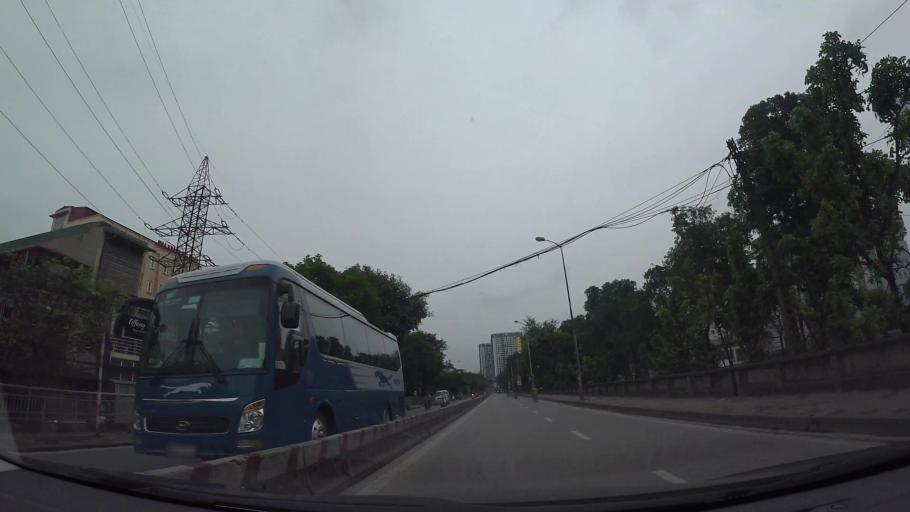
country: VN
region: Ha Noi
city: Hai BaTrung
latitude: 21.0176
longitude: 105.8622
